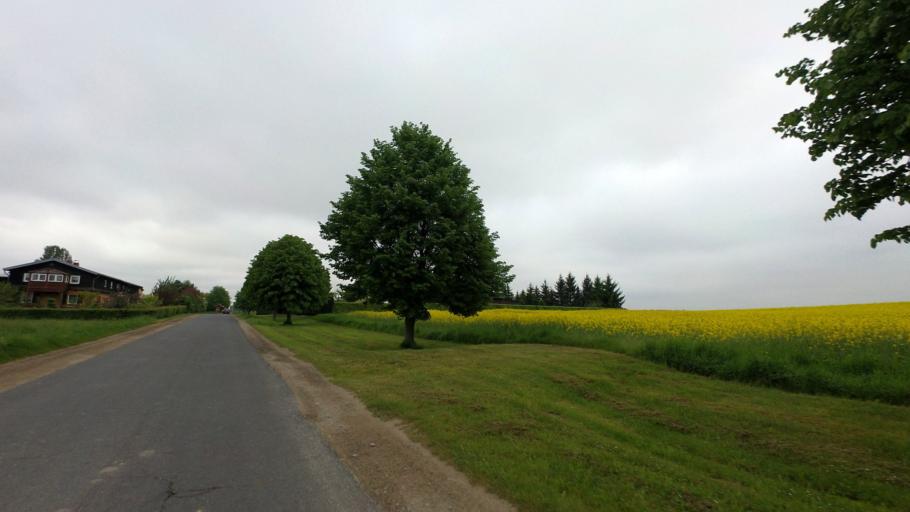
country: DE
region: Mecklenburg-Vorpommern
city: Mollenhagen
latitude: 53.6023
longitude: 12.9317
